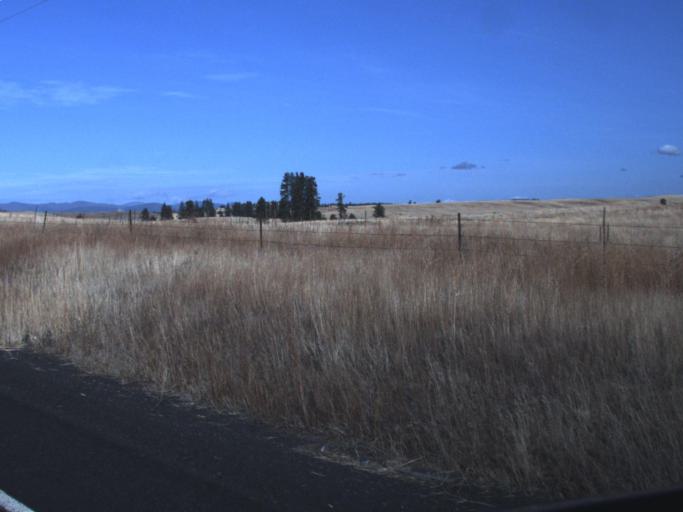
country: US
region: Washington
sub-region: Lincoln County
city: Davenport
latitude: 47.7502
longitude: -118.1726
